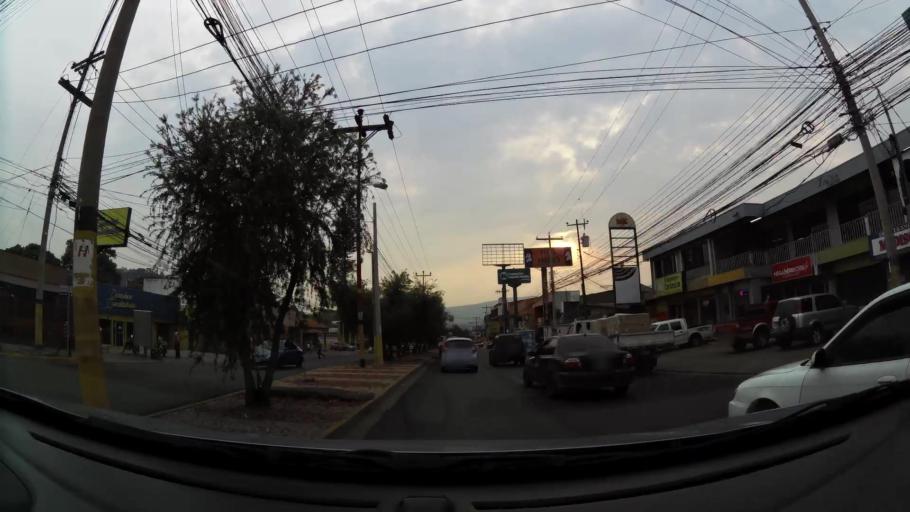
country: HN
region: Francisco Morazan
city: Tegucigalpa
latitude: 14.0998
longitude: -87.1949
